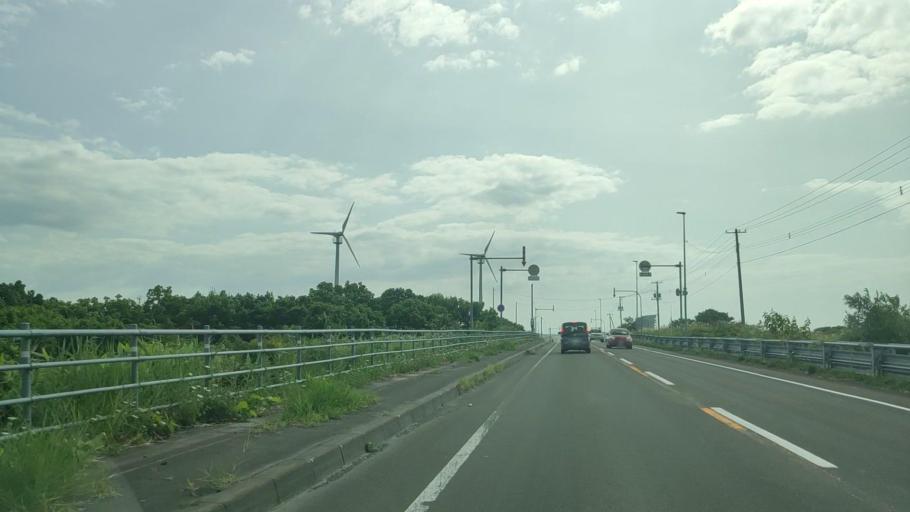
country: JP
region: Hokkaido
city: Rumoi
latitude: 44.3417
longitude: 141.6858
